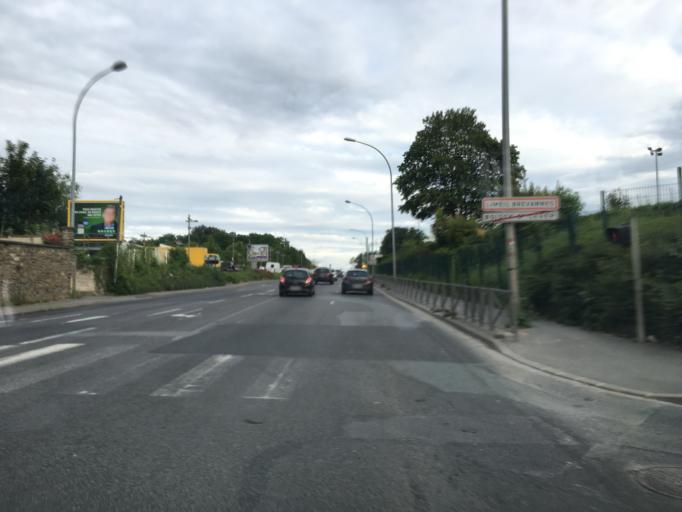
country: FR
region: Ile-de-France
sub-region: Departement du Val-de-Marne
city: Boissy-Saint-Leger
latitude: 48.7469
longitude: 2.5101
